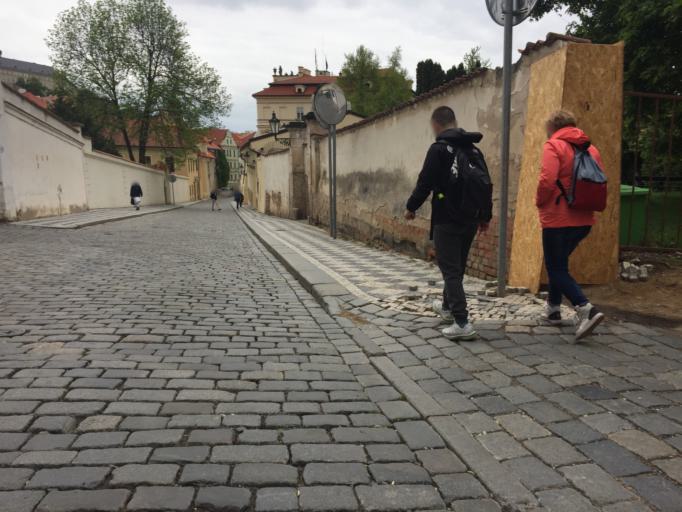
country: CZ
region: Praha
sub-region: Praha 1
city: Mala Strana
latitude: 50.0867
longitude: 14.3963
